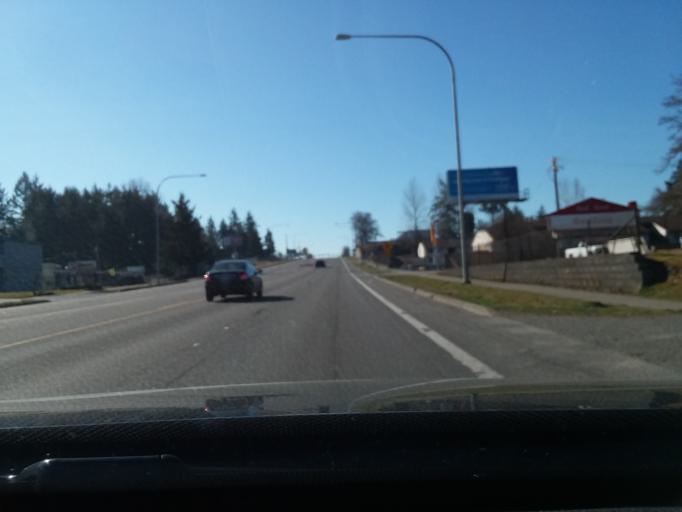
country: US
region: Washington
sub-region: Pierce County
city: Spanaway
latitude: 47.1284
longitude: -122.4349
